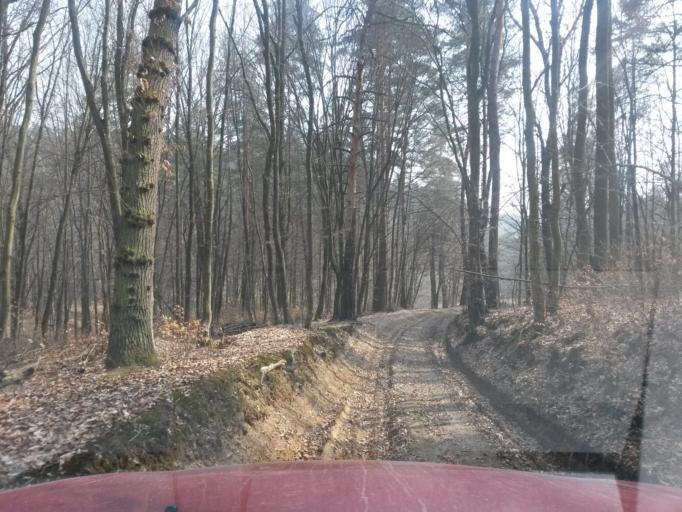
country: SK
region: Presovsky
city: Sabinov
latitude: 48.9698
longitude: 21.1019
